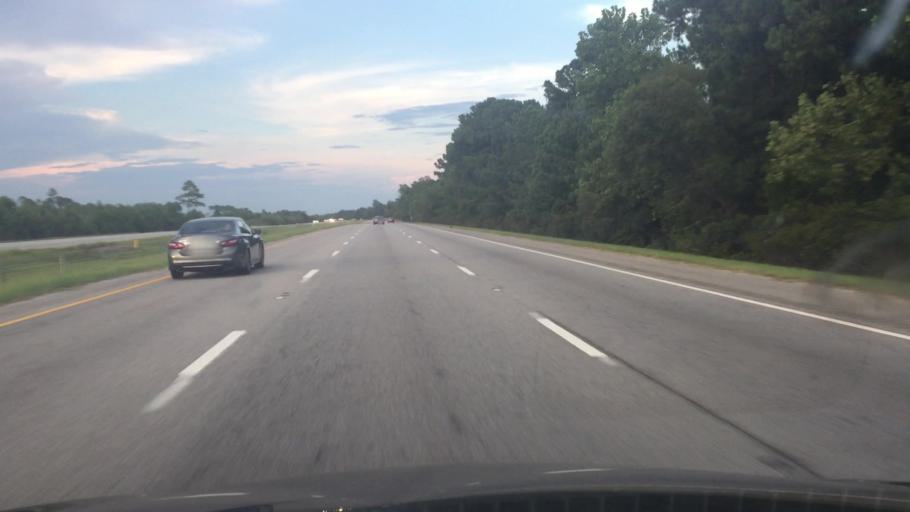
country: US
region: South Carolina
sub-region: Horry County
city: Myrtle Beach
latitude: 33.7676
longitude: -78.8293
